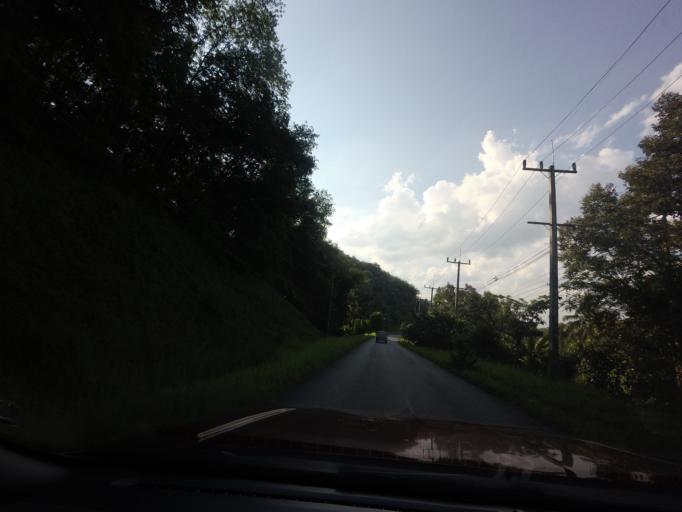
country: TH
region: Yala
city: Than To
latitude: 6.1733
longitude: 101.2663
